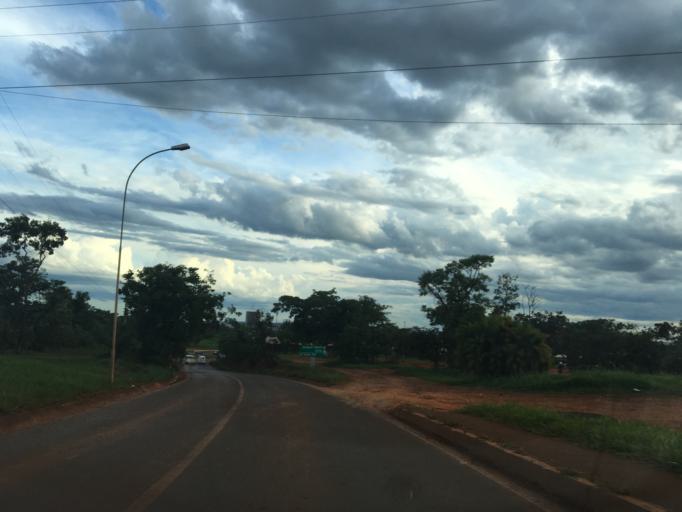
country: BR
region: Federal District
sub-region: Brasilia
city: Brasilia
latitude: -15.8335
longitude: -47.9321
